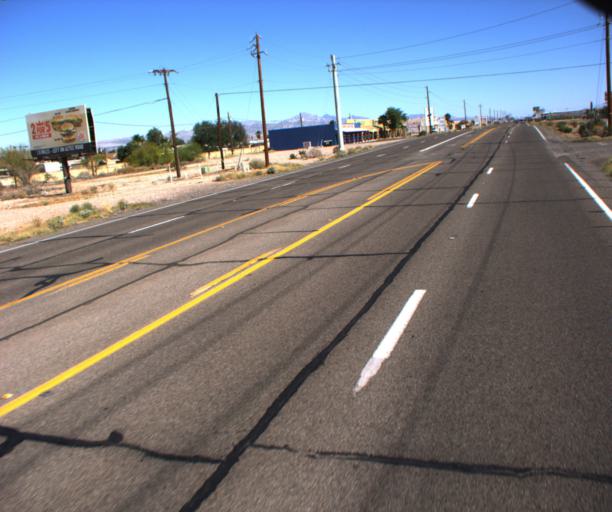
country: US
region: Arizona
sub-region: Mohave County
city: Mohave Valley
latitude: 34.9893
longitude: -114.5979
